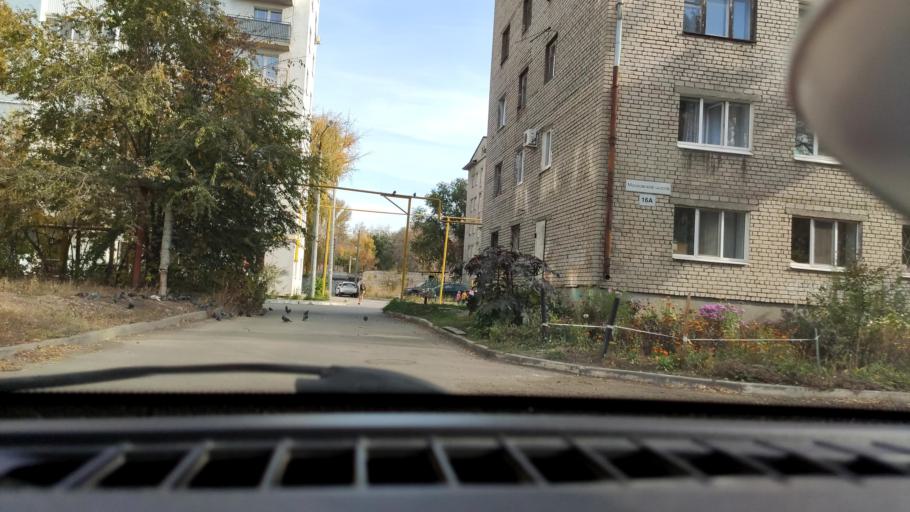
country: RU
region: Samara
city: Samara
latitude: 53.2080
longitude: 50.1657
